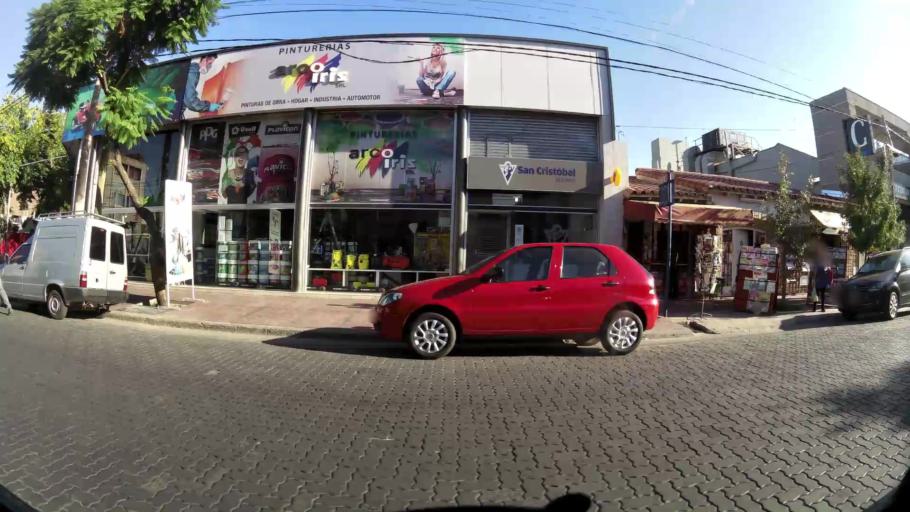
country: AR
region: Mendoza
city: Mendoza
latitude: -32.8999
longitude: -68.8291
